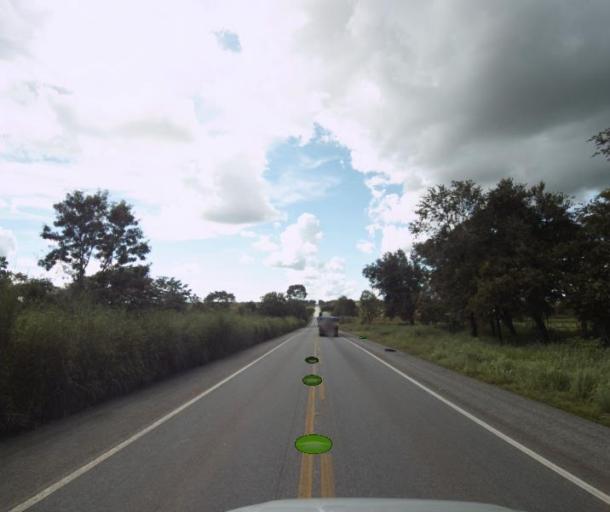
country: BR
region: Goias
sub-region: Porangatu
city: Porangatu
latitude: -13.1521
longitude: -49.1829
